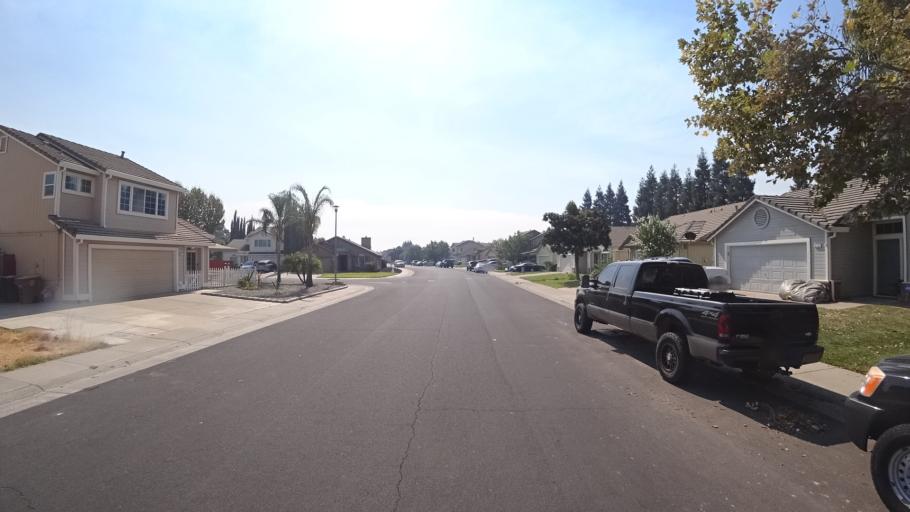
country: US
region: California
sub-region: Sacramento County
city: Laguna
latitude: 38.4246
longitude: -121.4106
